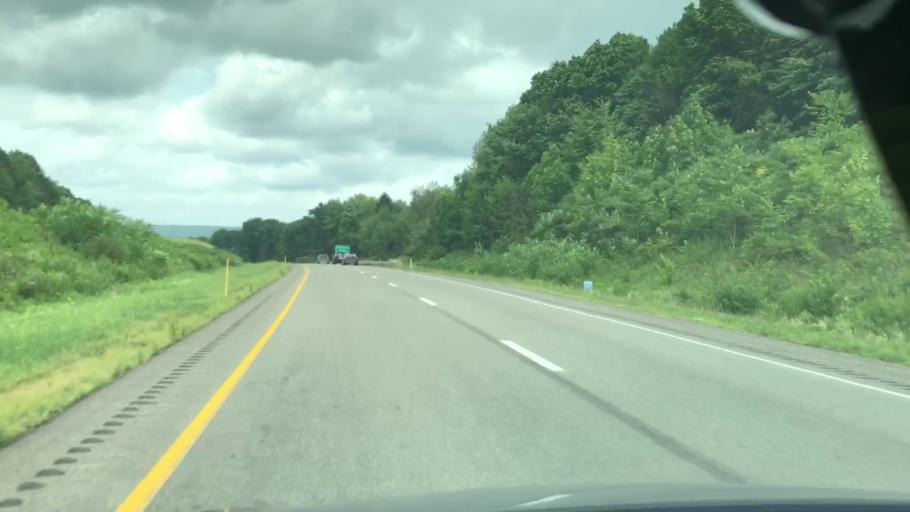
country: US
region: Pennsylvania
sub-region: Crawford County
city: Meadville
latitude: 41.6008
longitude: -80.1655
